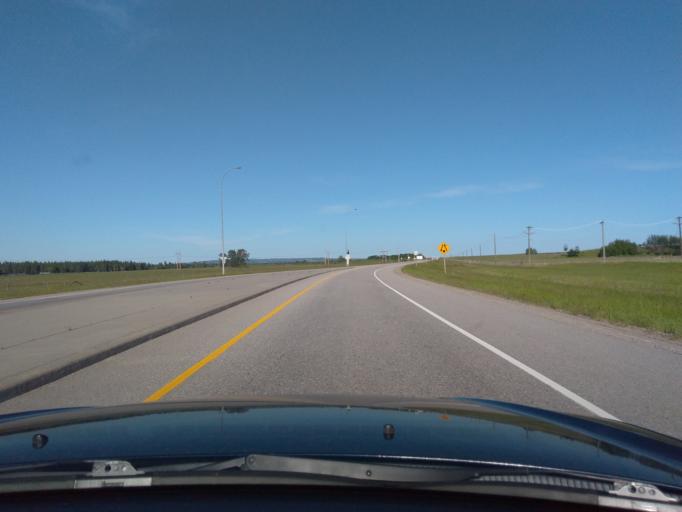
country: CA
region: Alberta
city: Cochrane
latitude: 51.0234
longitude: -114.4632
